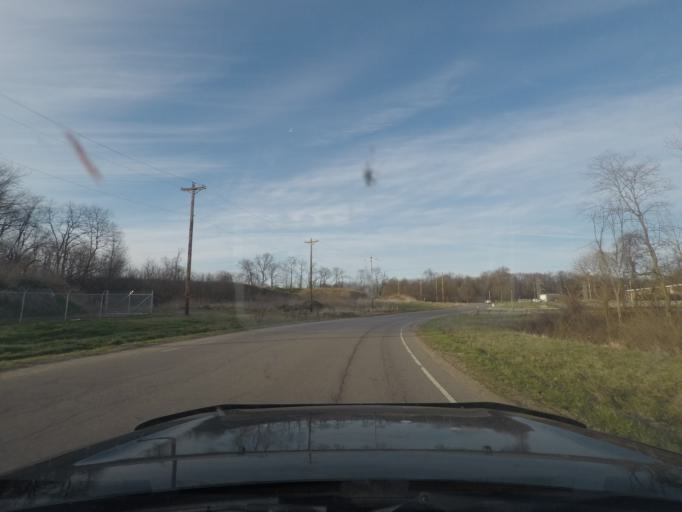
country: US
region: Indiana
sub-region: LaPorte County
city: LaPorte
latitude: 41.5992
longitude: -86.7492
